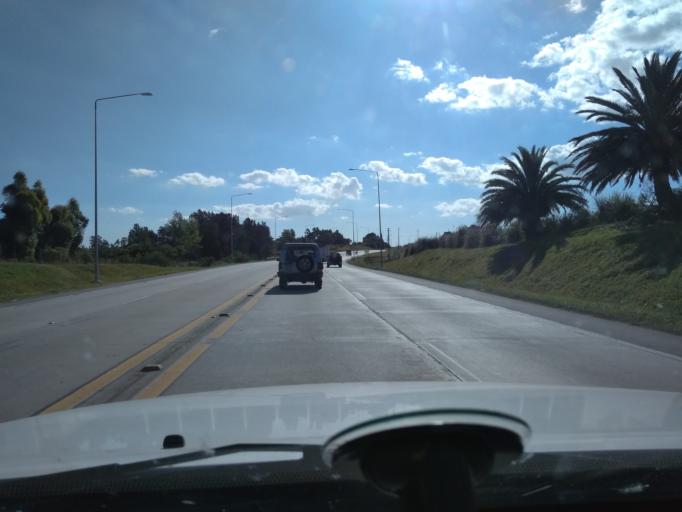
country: UY
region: Canelones
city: La Paz
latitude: -34.7826
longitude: -56.2456
